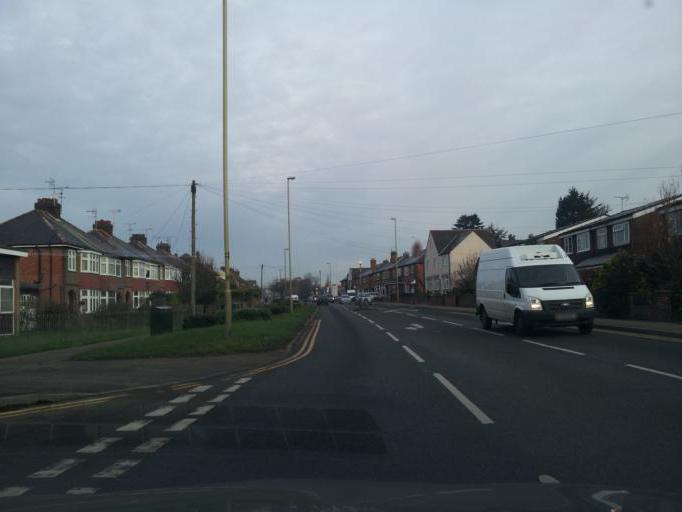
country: GB
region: England
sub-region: Leicestershire
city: Lutterworth
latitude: 52.4581
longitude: -1.1990
